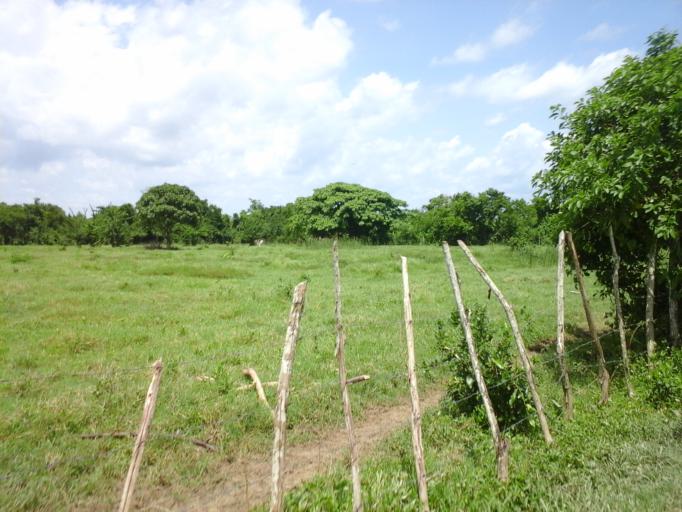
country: CO
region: Bolivar
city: San Pablo
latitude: 10.1527
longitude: -75.2732
